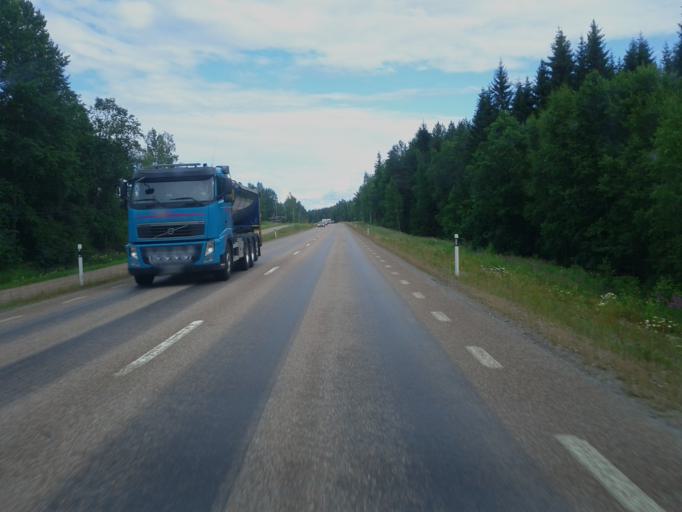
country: SE
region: Dalarna
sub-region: Faluns Kommun
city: Bjursas
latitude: 60.7422
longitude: 15.4009
